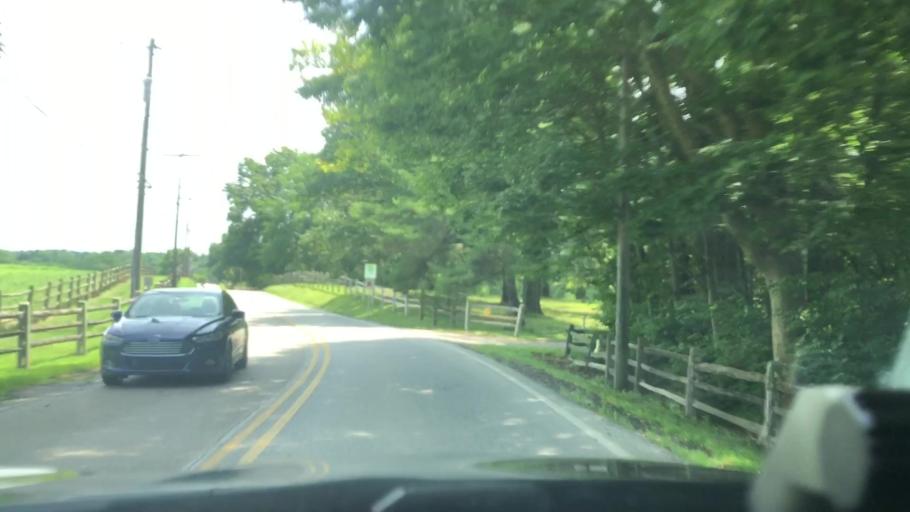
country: US
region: Pennsylvania
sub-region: Montgomery County
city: Flourtown
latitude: 40.0962
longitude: -75.2279
